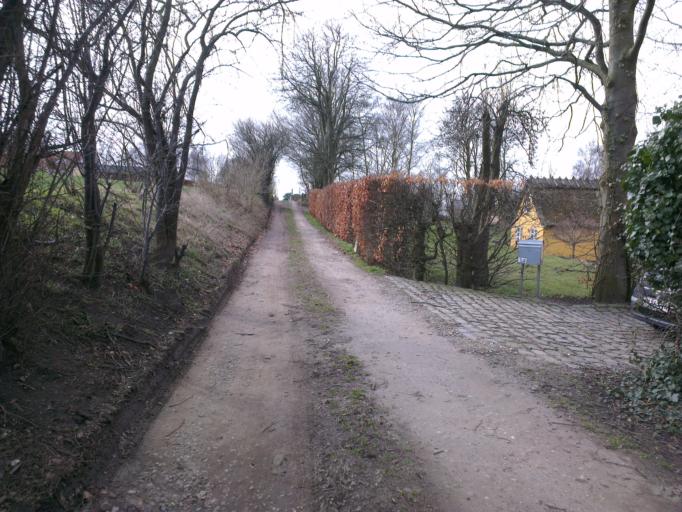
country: DK
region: Zealand
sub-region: Lejre Kommune
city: Ejby
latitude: 55.7817
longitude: 11.8646
